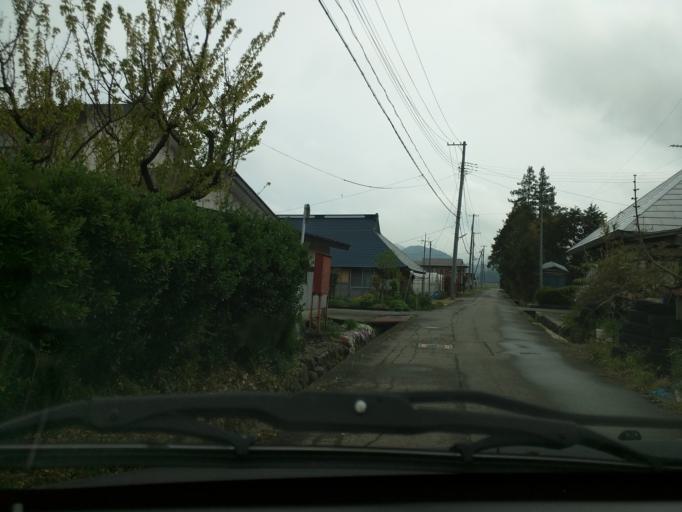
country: JP
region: Fukushima
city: Kitakata
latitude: 37.4427
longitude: 139.8804
